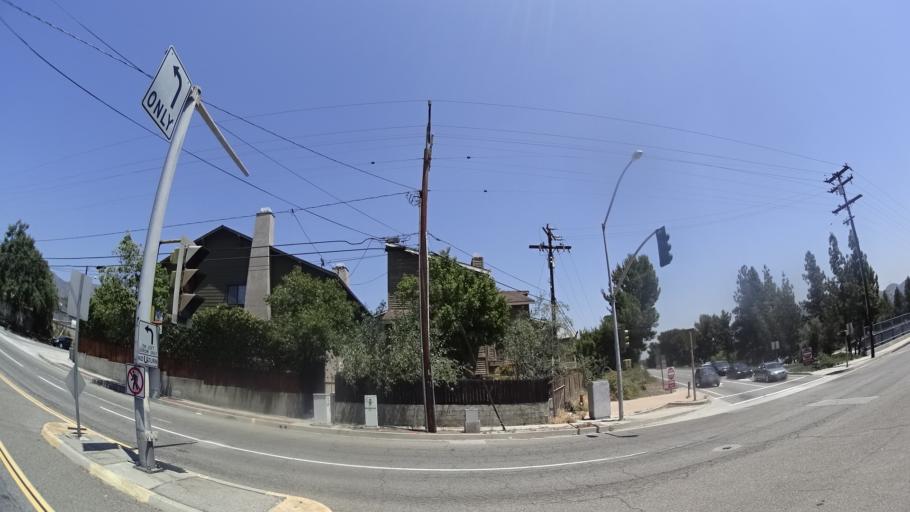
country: US
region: California
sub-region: Los Angeles County
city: La Crescenta-Montrose
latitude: 34.2127
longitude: -118.2280
